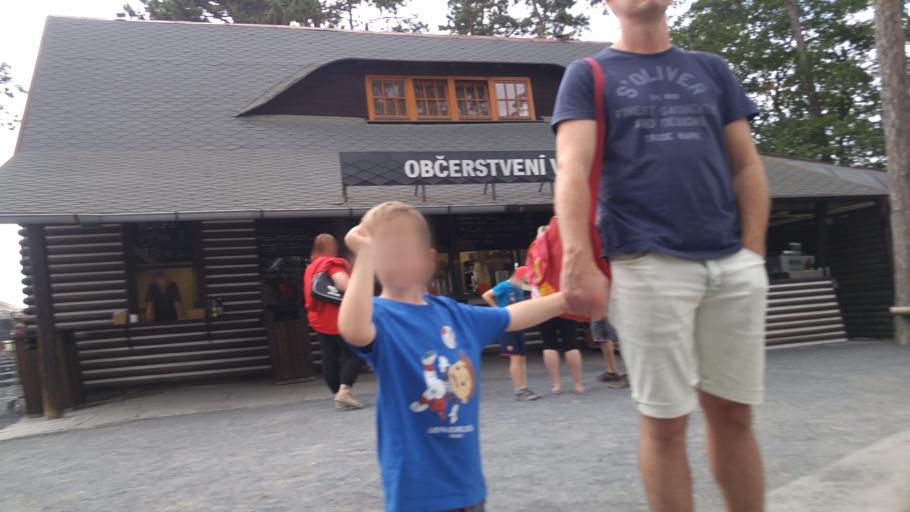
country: CZ
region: Praha
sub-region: Praha 1
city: Mala Strana
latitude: 50.1185
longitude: 14.4020
